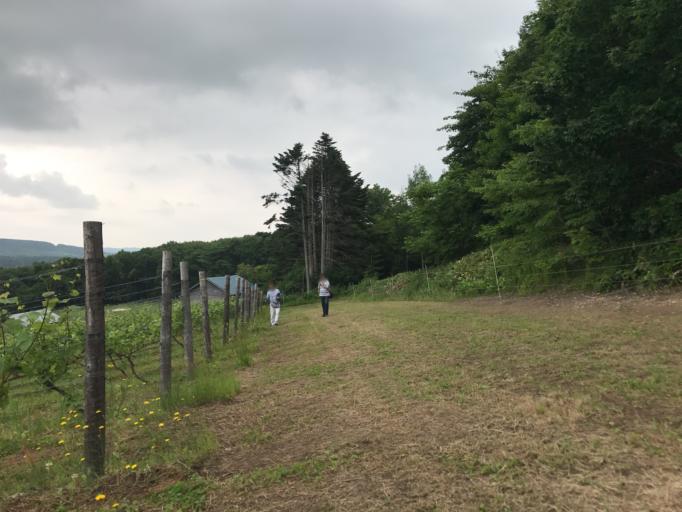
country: JP
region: Hokkaido
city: Iwamizawa
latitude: 43.1914
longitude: 141.8174
